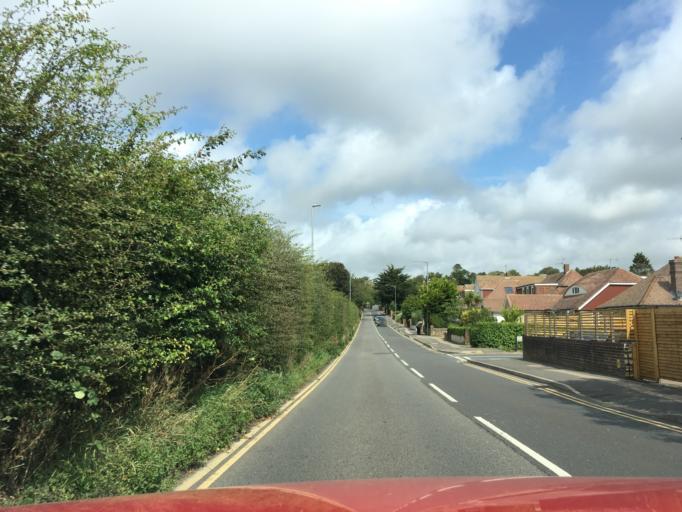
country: GB
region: England
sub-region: Brighton and Hove
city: Rottingdean
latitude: 50.8291
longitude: -0.0728
